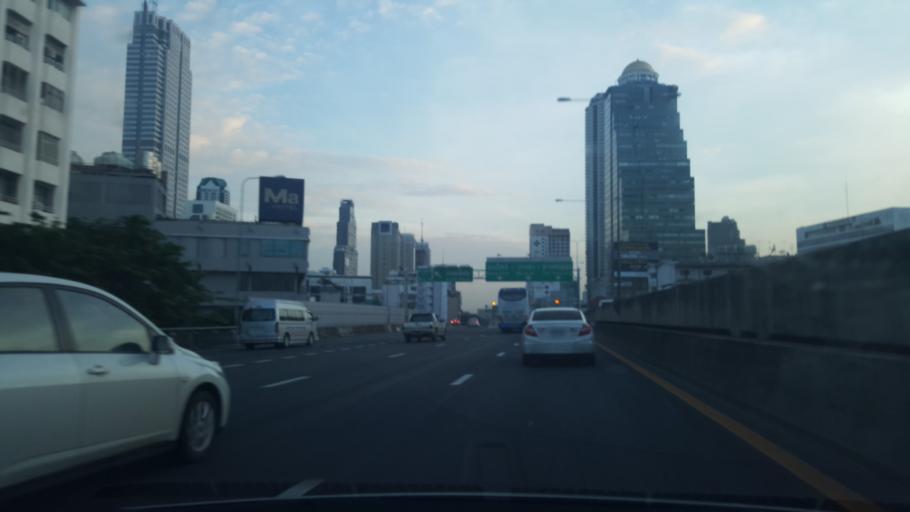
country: TH
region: Bangkok
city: Samphanthawong
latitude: 13.7267
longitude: 100.5175
